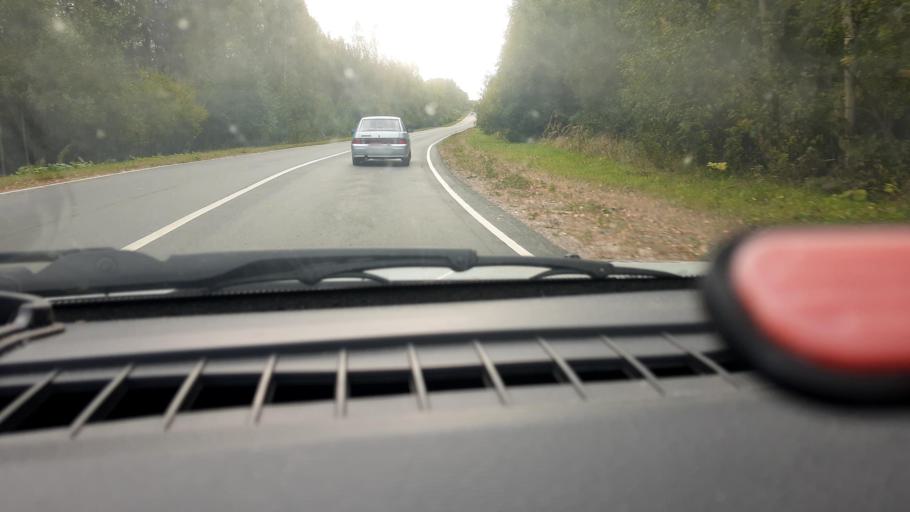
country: RU
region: Nizjnij Novgorod
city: Uren'
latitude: 57.2480
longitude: 45.6007
